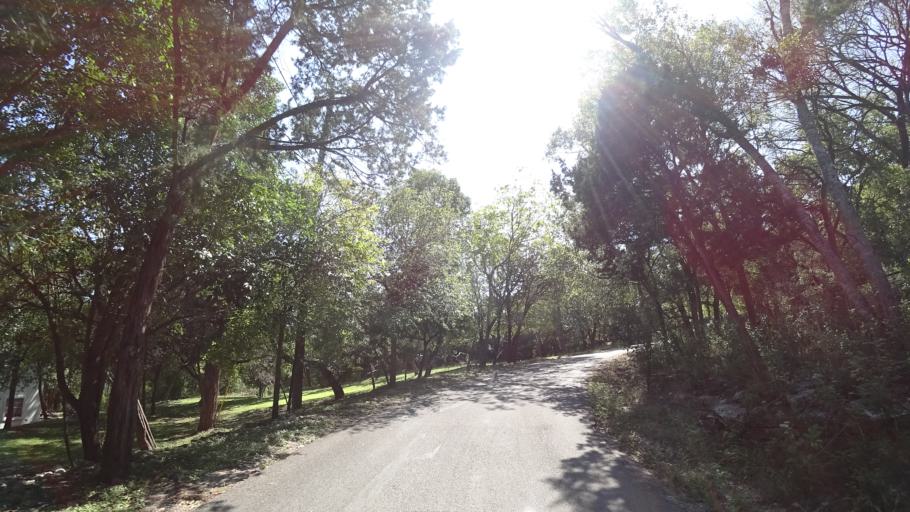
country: US
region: Texas
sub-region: Travis County
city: West Lake Hills
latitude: 30.3051
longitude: -97.7975
